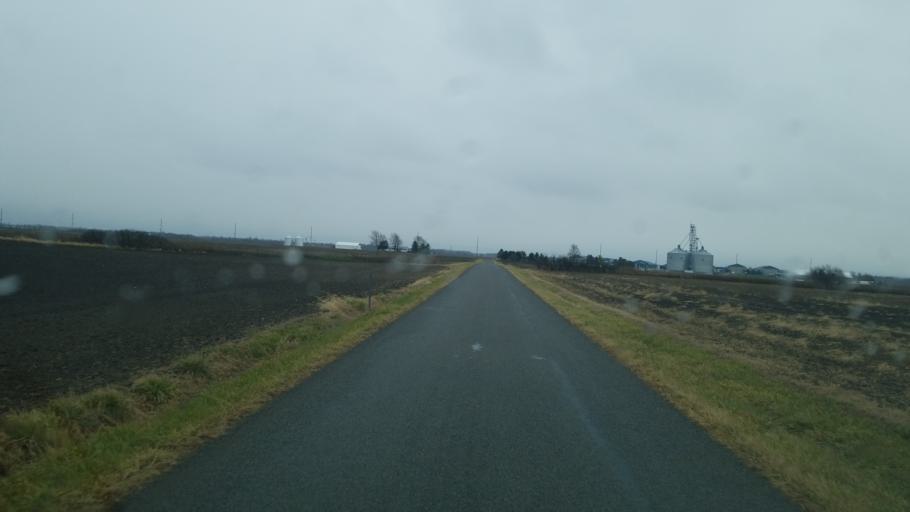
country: US
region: Ohio
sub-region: Logan County
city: Northwood
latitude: 40.4393
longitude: -83.5644
